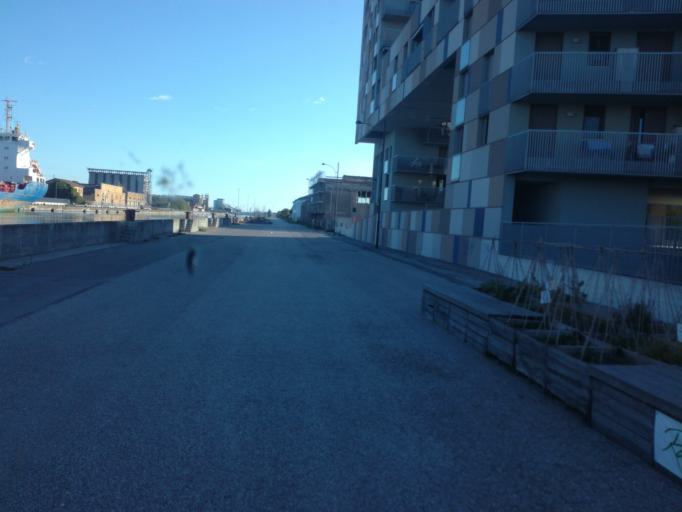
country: IT
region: Emilia-Romagna
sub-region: Provincia di Ravenna
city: Ravenna
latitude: 44.4223
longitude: 12.2144
